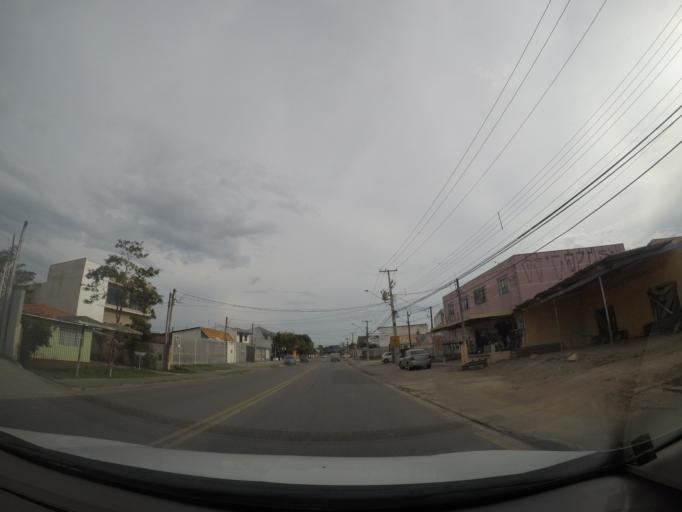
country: BR
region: Parana
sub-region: Sao Jose Dos Pinhais
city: Sao Jose dos Pinhais
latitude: -25.4977
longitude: -49.2178
